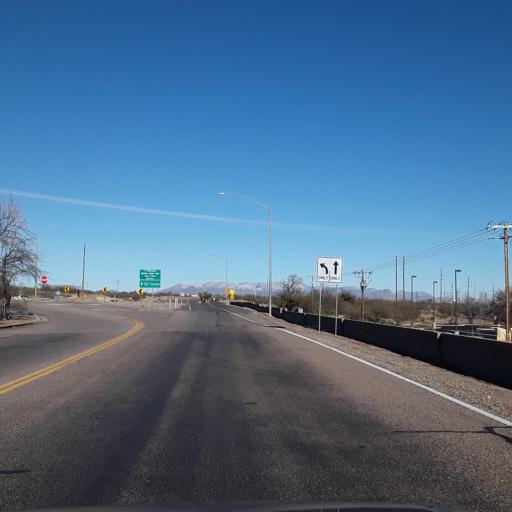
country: US
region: Arizona
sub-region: Cochise County
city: Sierra Vista
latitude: 31.5598
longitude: -110.3078
